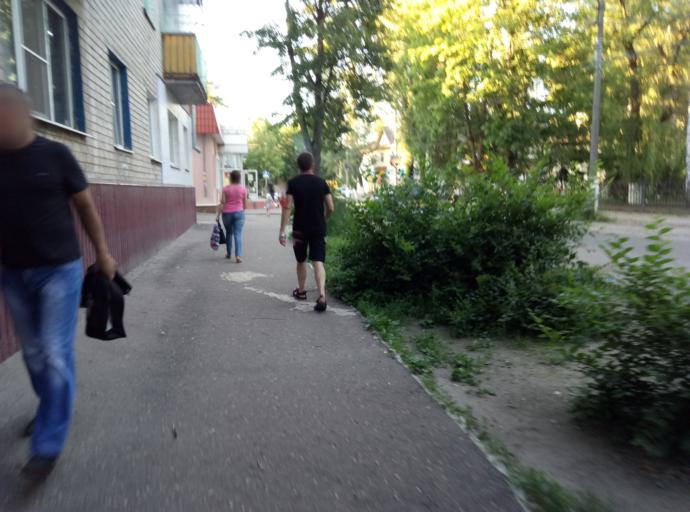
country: RU
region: Kursk
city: Kursk
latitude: 51.6715
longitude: 36.1512
